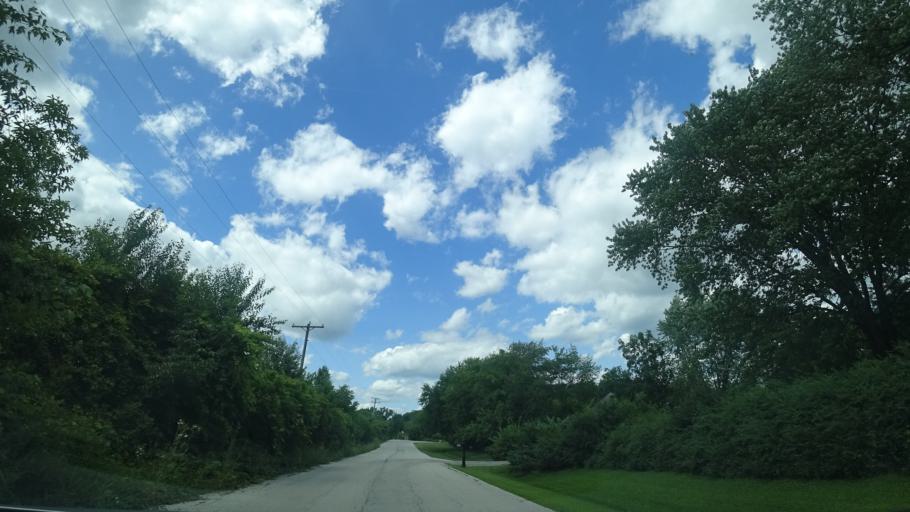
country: US
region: Illinois
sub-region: Will County
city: Homer Glen
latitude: 41.5969
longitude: -87.9058
